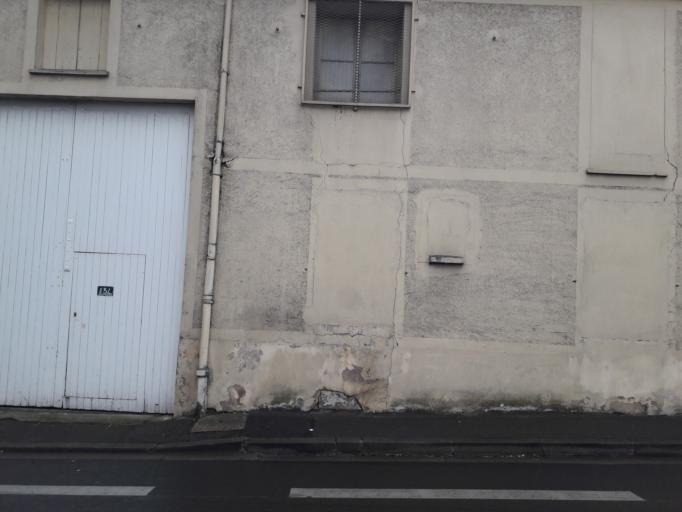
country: FR
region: Ile-de-France
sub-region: Departement de l'Essonne
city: Epinay-sur-Orge
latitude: 48.6829
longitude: 2.3105
